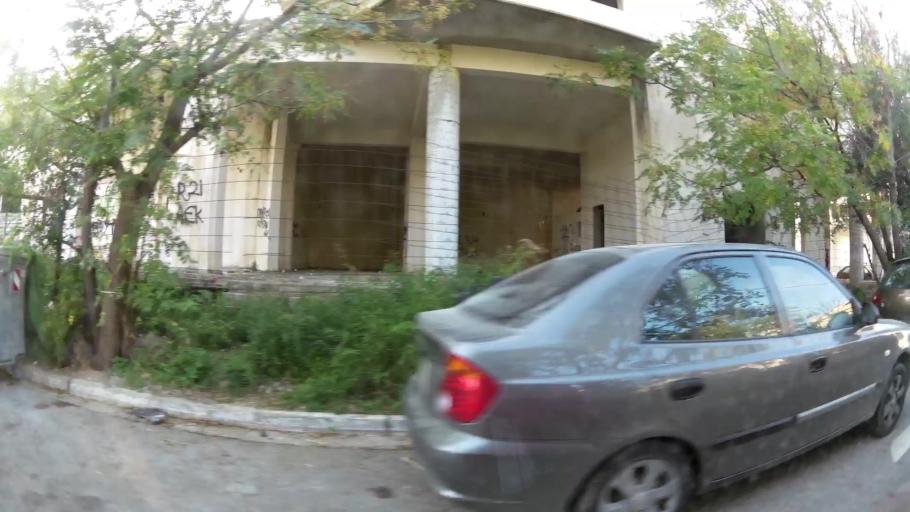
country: GR
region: Attica
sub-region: Nomarchia Anatolikis Attikis
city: Acharnes
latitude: 38.0854
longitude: 23.7394
